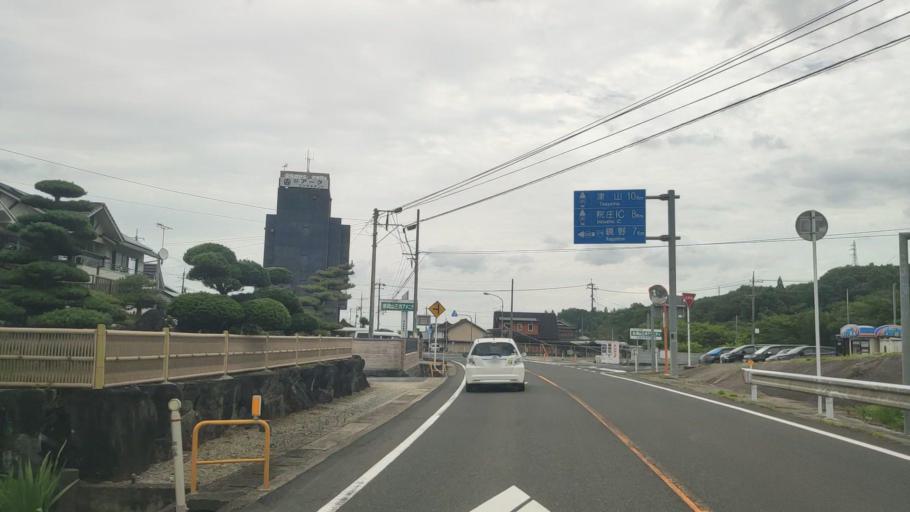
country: JP
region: Okayama
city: Tsuyama
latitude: 35.0613
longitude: 133.8735
